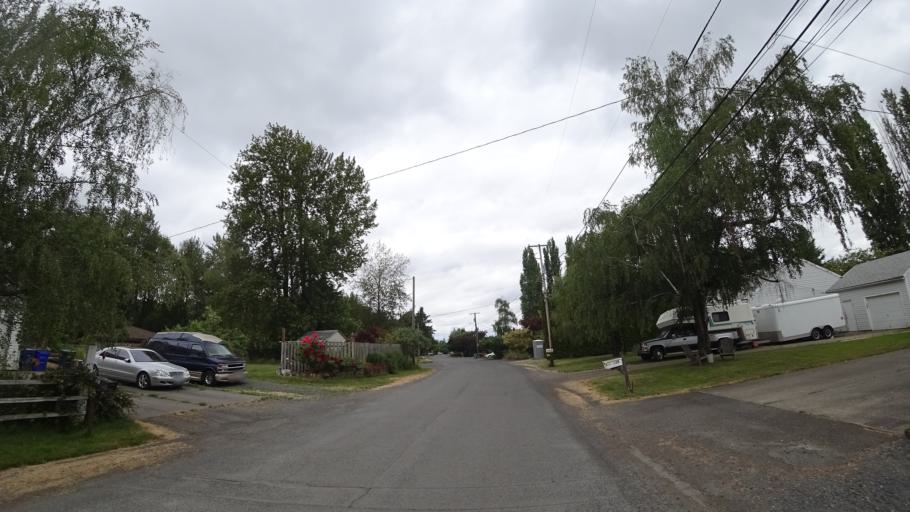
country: US
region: Washington
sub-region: Clark County
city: Vancouver
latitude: 45.5931
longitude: -122.6534
